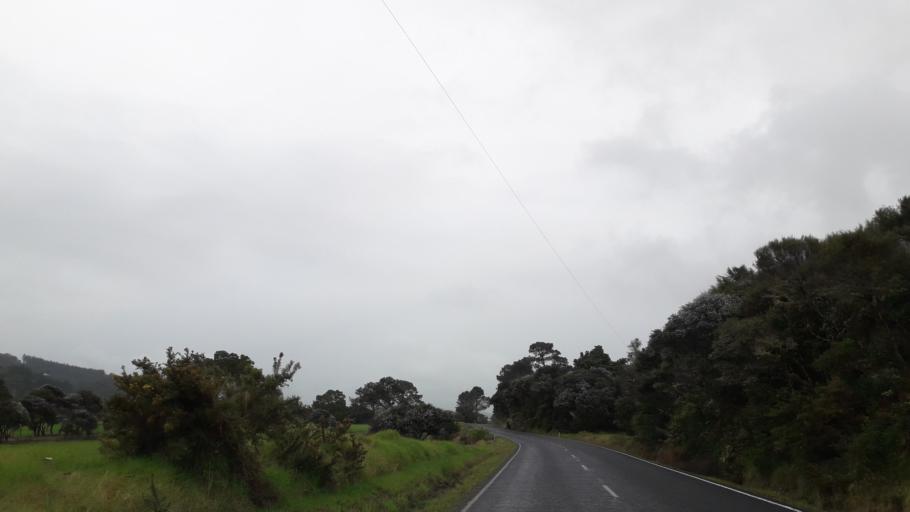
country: NZ
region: Northland
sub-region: Far North District
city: Kaitaia
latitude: -35.3645
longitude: 173.4957
